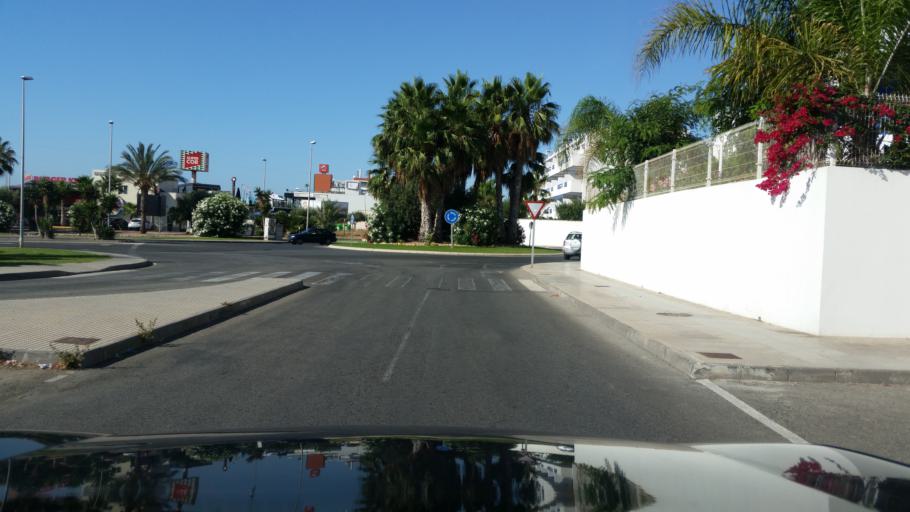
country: ES
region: Valencia
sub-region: Provincia de Alicante
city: Torrevieja
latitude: 37.9382
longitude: -0.7215
